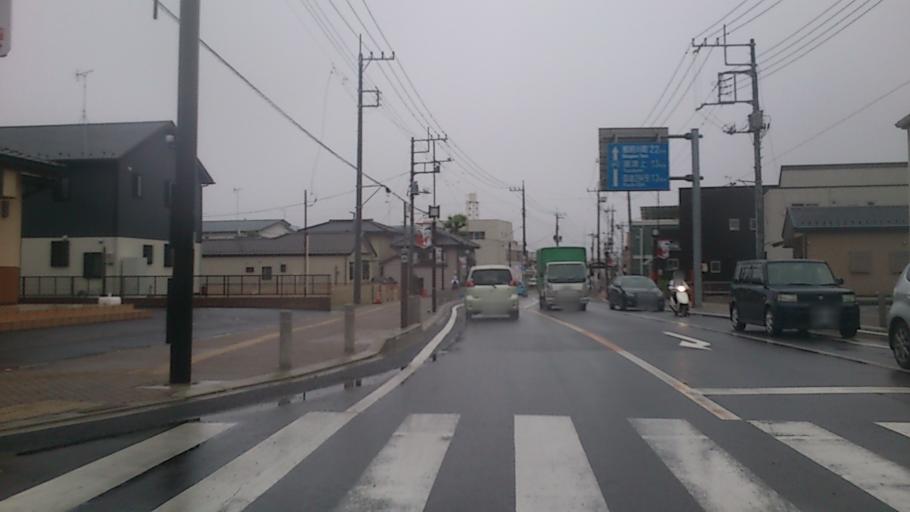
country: JP
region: Tochigi
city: Otawara
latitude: 36.8668
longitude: 140.0280
